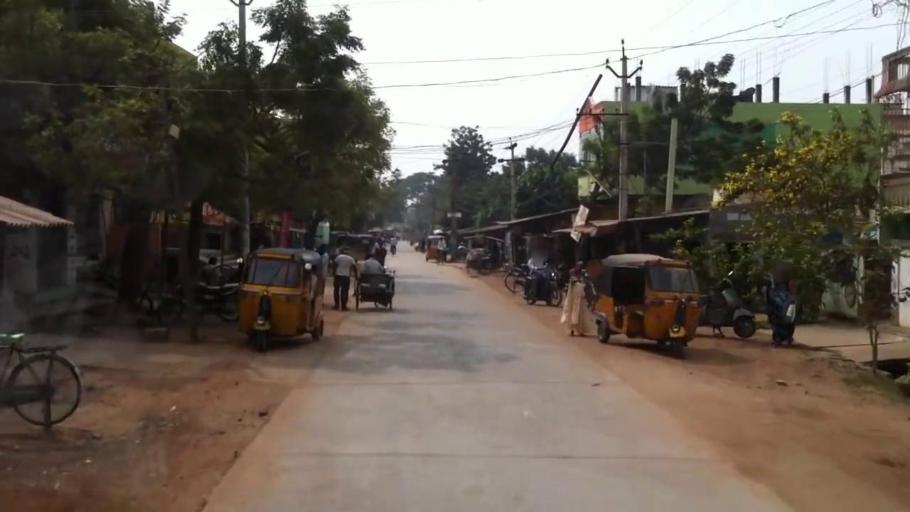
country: IN
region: Andhra Pradesh
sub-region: Guntur
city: Bhattiprolu
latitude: 16.2249
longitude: 80.6526
